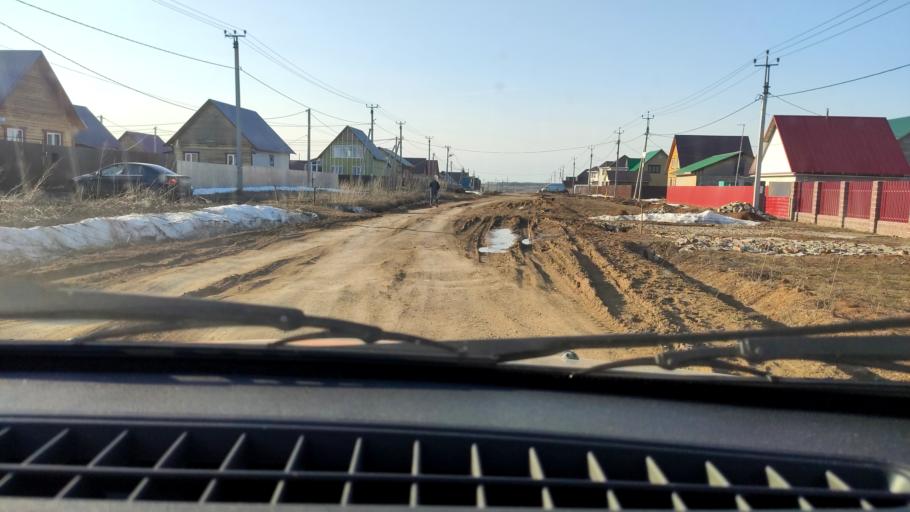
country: RU
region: Bashkortostan
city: Iglino
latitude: 54.8207
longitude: 56.4421
